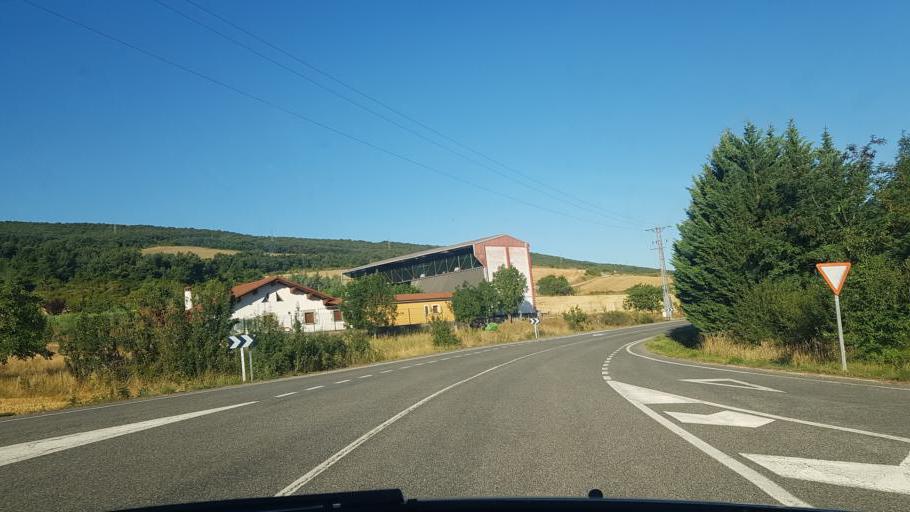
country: ES
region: Navarre
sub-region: Provincia de Navarra
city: Elorz
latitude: 42.7554
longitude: -1.5481
